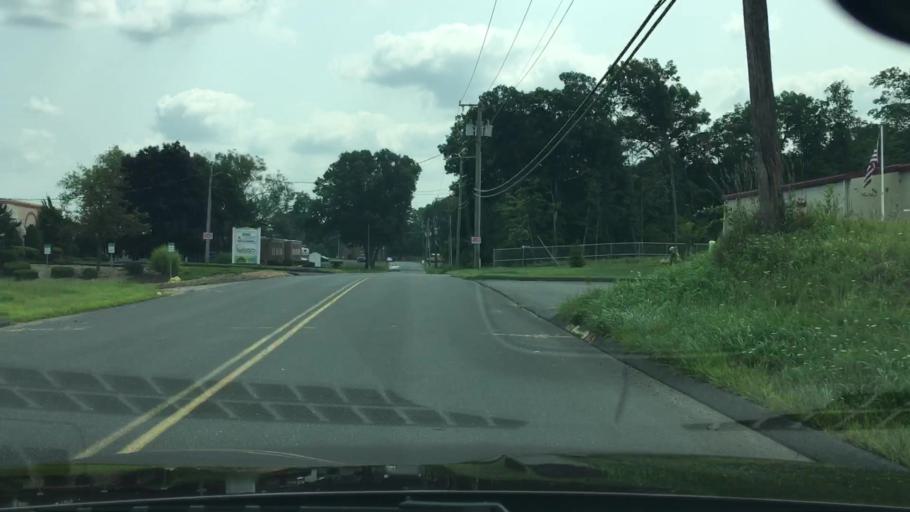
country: US
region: Connecticut
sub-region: New Haven County
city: Cheshire Village
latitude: 41.5337
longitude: -72.8993
